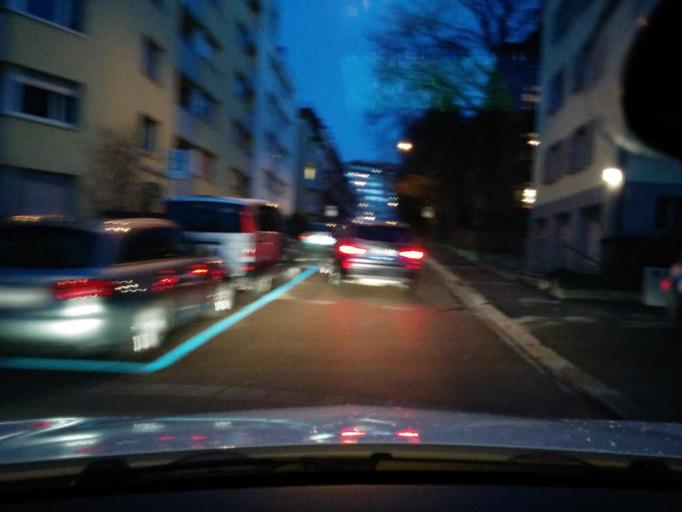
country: CH
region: Zurich
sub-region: Bezirk Zuerich
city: Zuerich (Kreis 11) / Oerlikon
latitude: 47.4095
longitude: 8.5406
